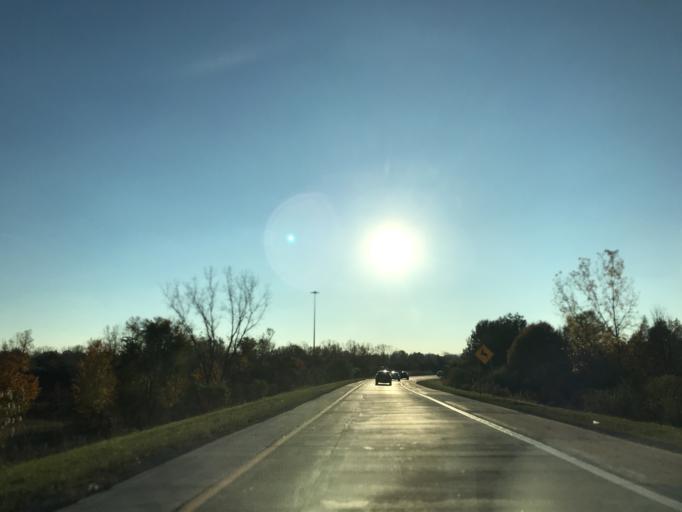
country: US
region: Michigan
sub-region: Oakland County
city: Novi
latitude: 42.4877
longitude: -83.4309
